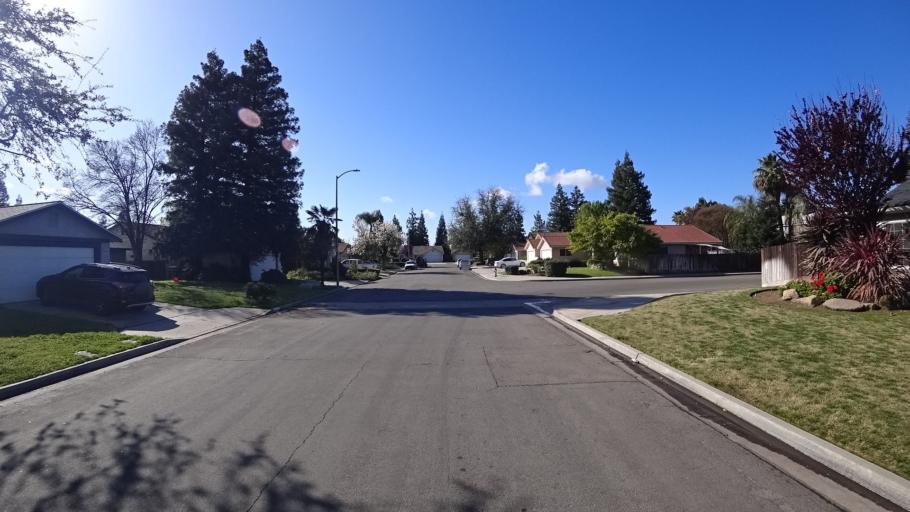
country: US
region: California
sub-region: Fresno County
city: West Park
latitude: 36.8236
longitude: -119.8736
